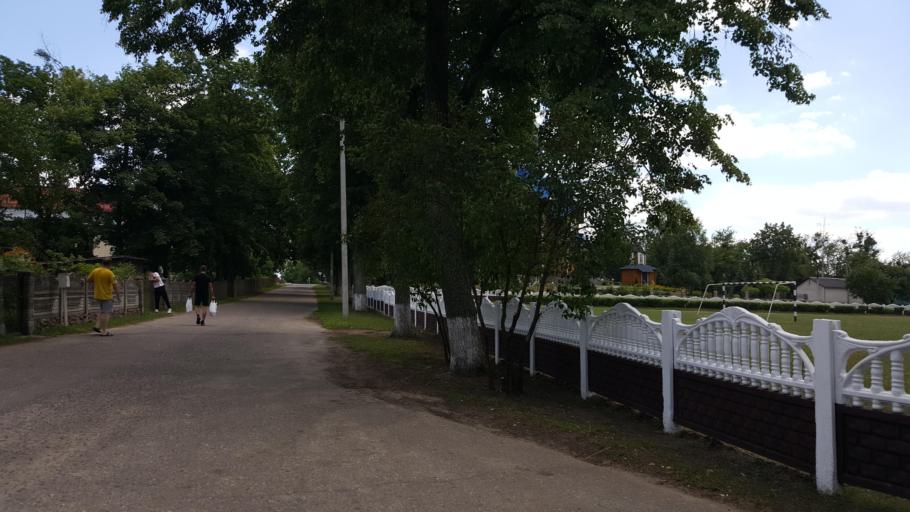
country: BY
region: Brest
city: Kamyanyuki
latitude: 52.5593
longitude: 23.7947
